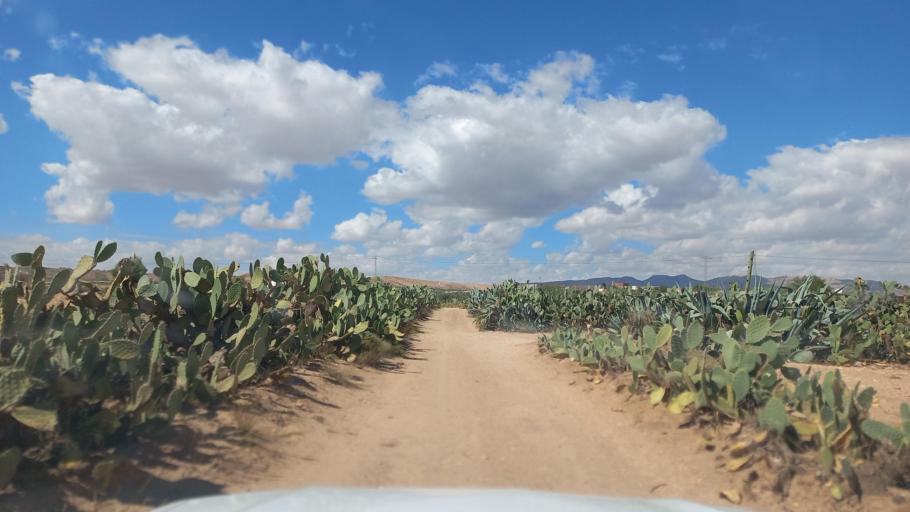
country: TN
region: Al Qasrayn
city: Sbiba
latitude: 35.3557
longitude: 9.0183
